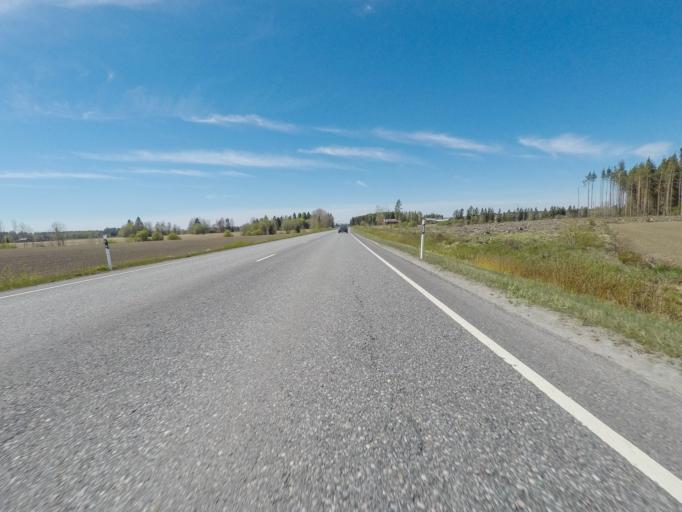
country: FI
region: Haeme
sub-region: Forssa
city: Humppila
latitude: 60.9572
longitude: 23.3590
